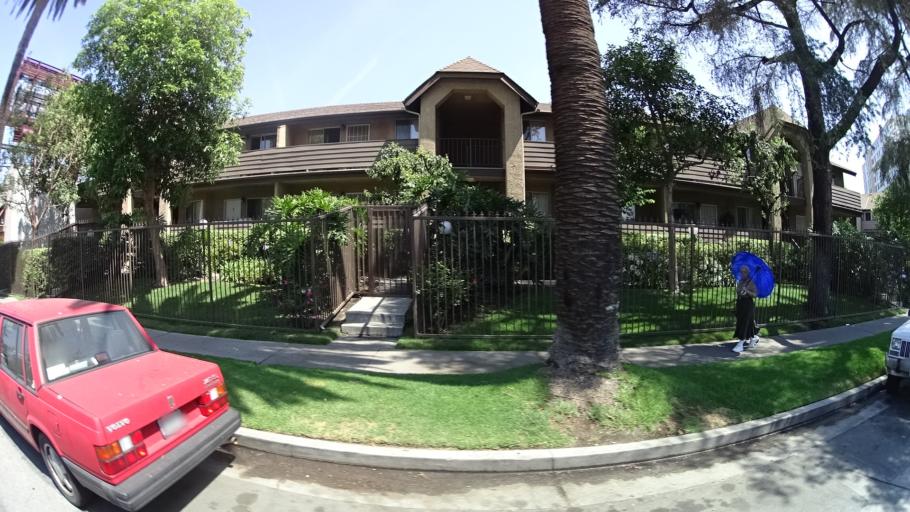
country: US
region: California
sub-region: Los Angeles County
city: Van Nuys
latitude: 34.2013
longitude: -118.4566
